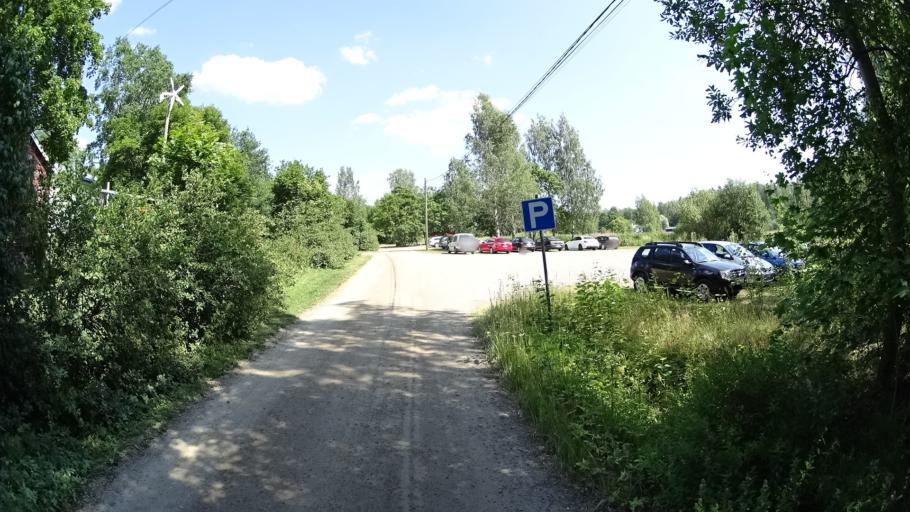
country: FI
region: Uusimaa
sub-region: Porvoo
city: Porvoo
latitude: 60.4024
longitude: 25.7293
